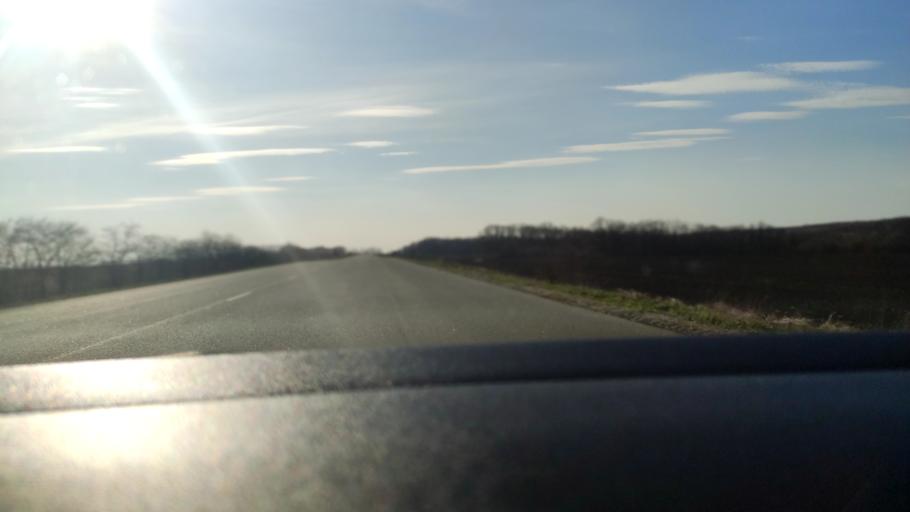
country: RU
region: Voronezj
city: Kolodeznyy
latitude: 51.3392
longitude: 39.0528
